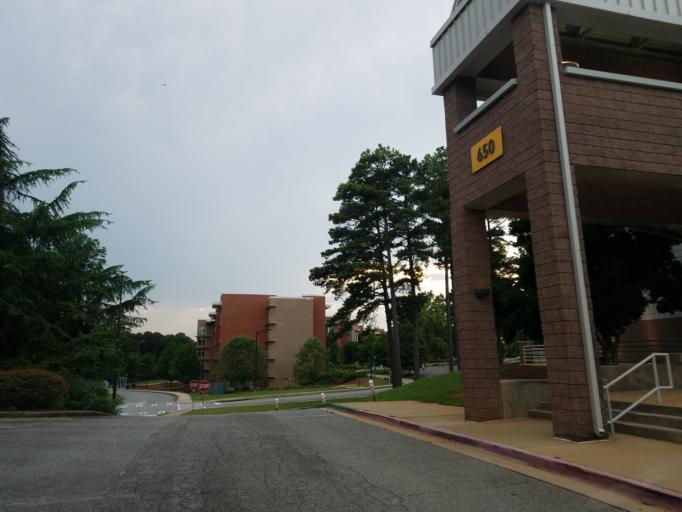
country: US
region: Georgia
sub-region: Cobb County
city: Fair Oaks
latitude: 33.9363
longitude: -84.5197
